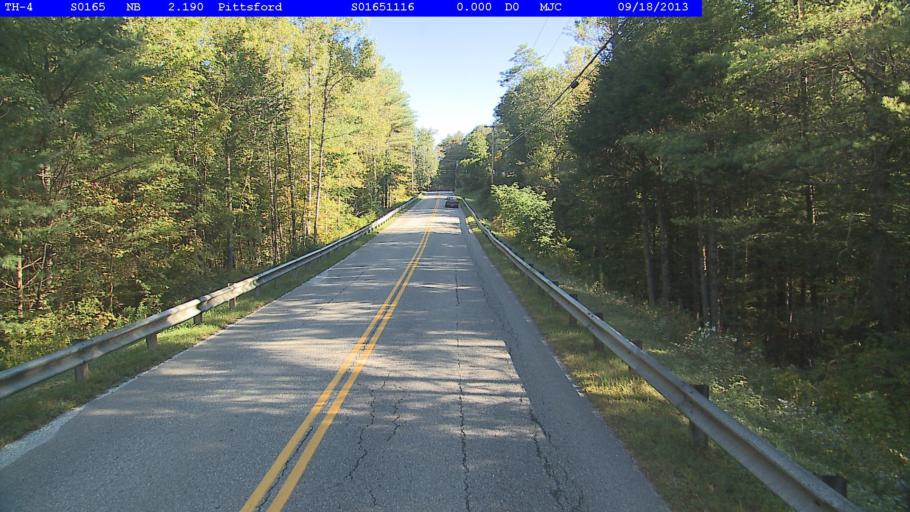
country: US
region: Vermont
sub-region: Rutland County
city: Rutland
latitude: 43.6698
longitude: -72.9432
